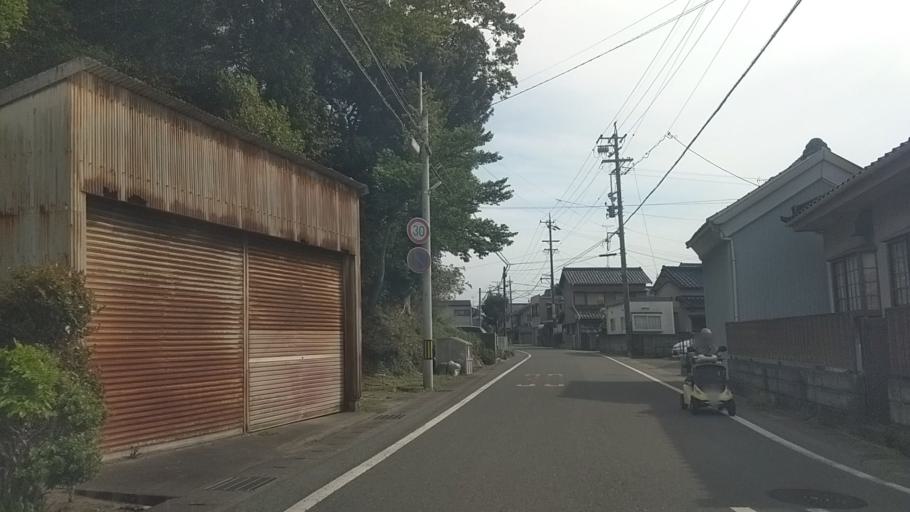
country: JP
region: Shizuoka
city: Kosai-shi
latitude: 34.7042
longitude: 137.6298
